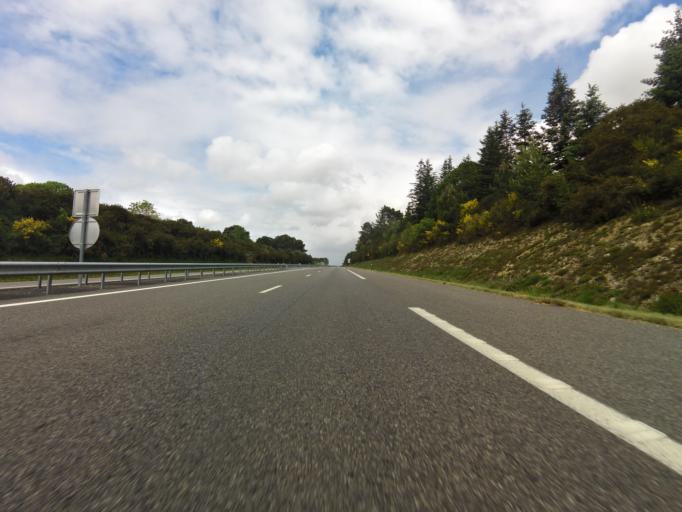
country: FR
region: Brittany
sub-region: Departement du Morbihan
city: Allaire
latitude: 47.6155
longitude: -2.1517
